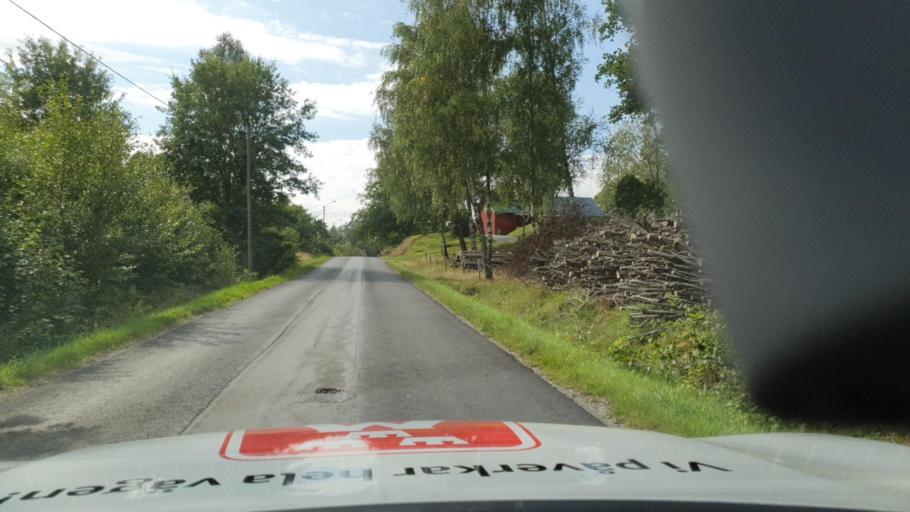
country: SE
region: Vaestra Goetaland
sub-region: Marks Kommun
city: Kinna
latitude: 57.3891
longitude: 12.6925
